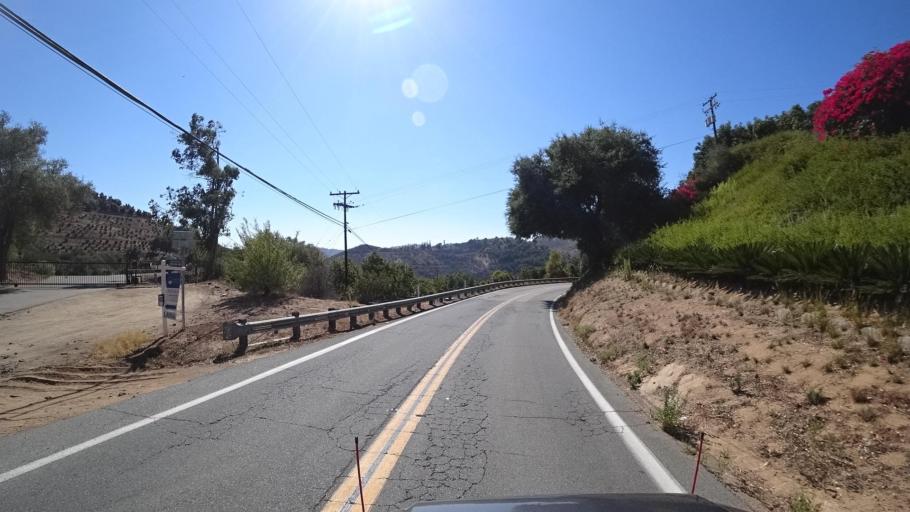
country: US
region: California
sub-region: San Diego County
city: Hidden Meadows
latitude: 33.2619
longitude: -117.1361
